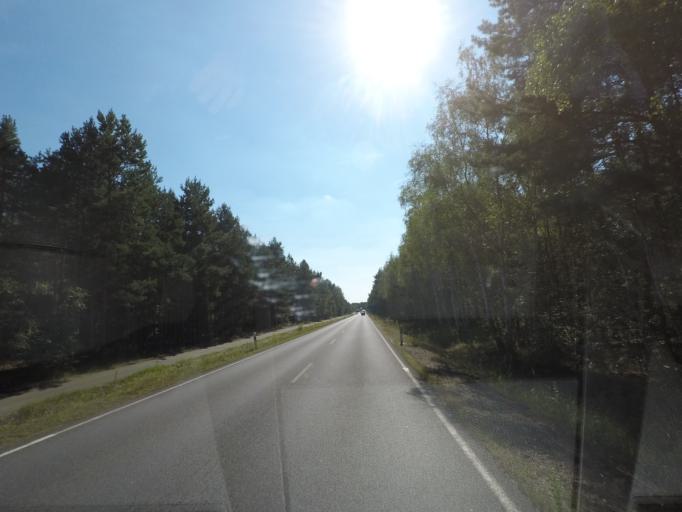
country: DE
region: Brandenburg
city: Schipkau
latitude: 51.4964
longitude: 13.8948
